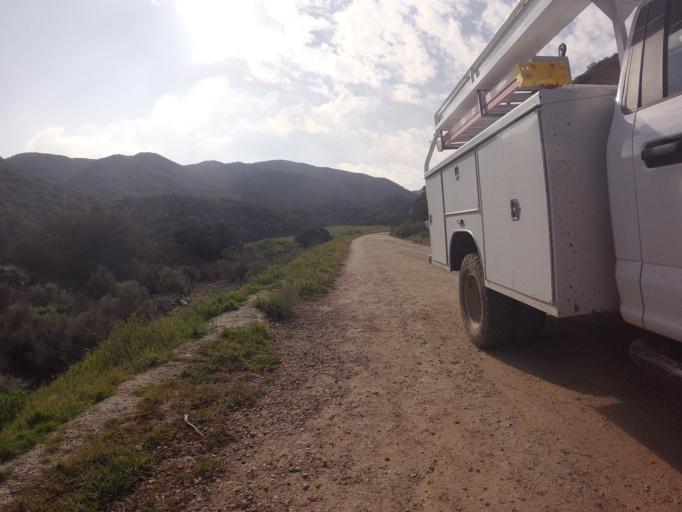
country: US
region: California
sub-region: Riverside County
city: Corona
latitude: 33.8368
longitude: -117.6022
